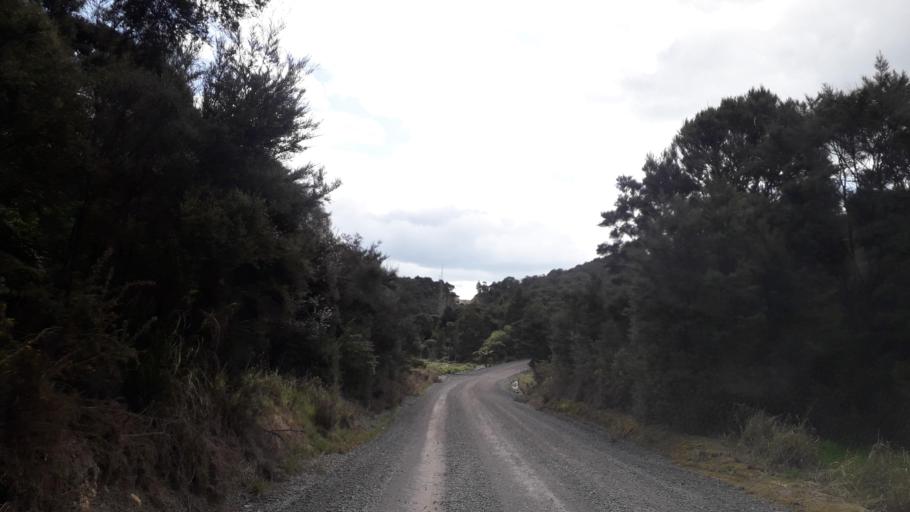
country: NZ
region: Northland
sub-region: Far North District
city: Paihia
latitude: -35.3085
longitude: 174.2214
